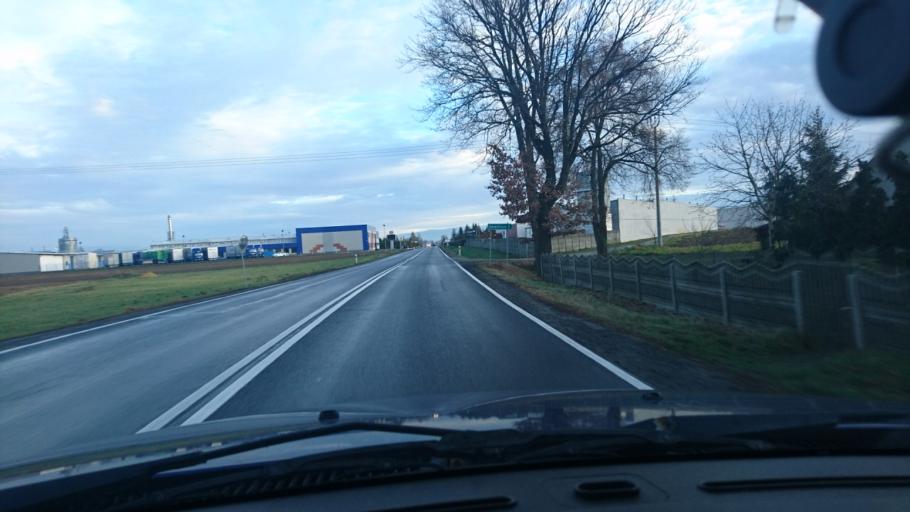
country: PL
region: Greater Poland Voivodeship
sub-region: Powiat kepinski
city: Leka Opatowska
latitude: 51.2301
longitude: 18.0767
